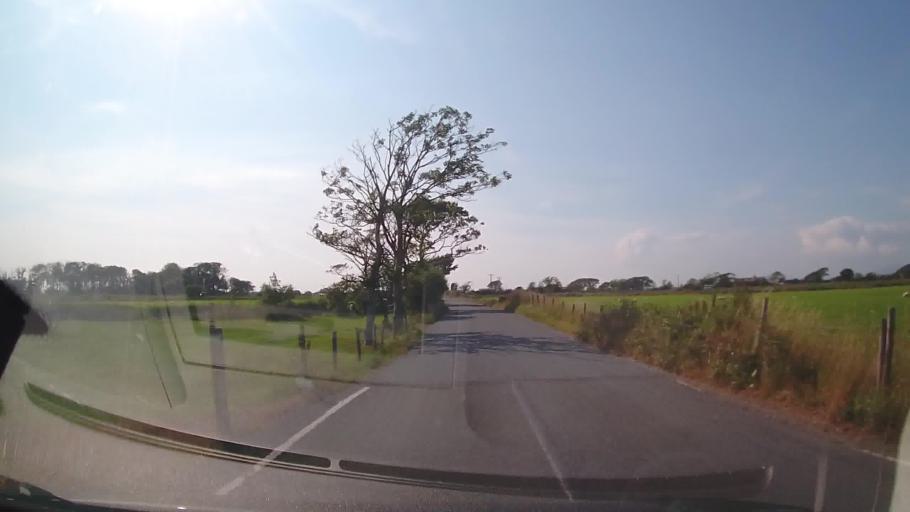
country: GB
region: Wales
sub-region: Gwynedd
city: Llanbedr
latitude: 52.8199
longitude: -4.1093
